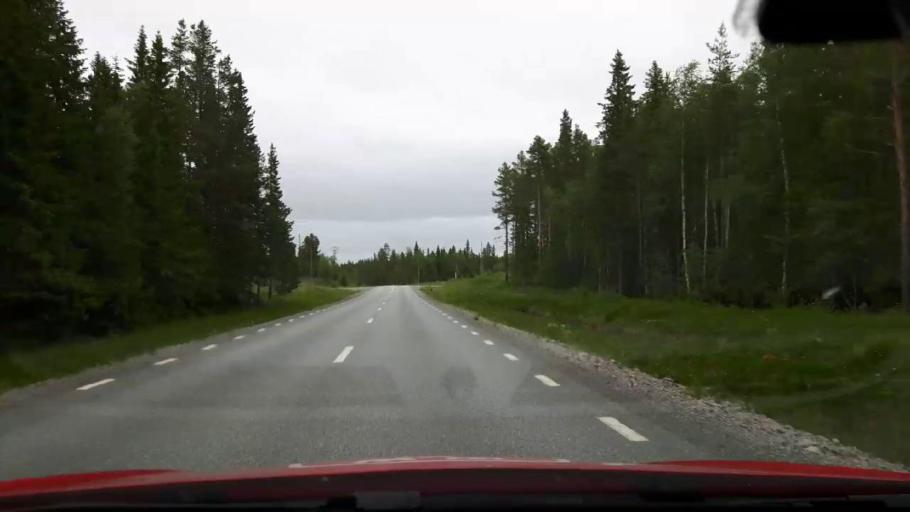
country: SE
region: Jaemtland
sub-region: OEstersunds Kommun
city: Lit
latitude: 63.6912
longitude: 14.6786
